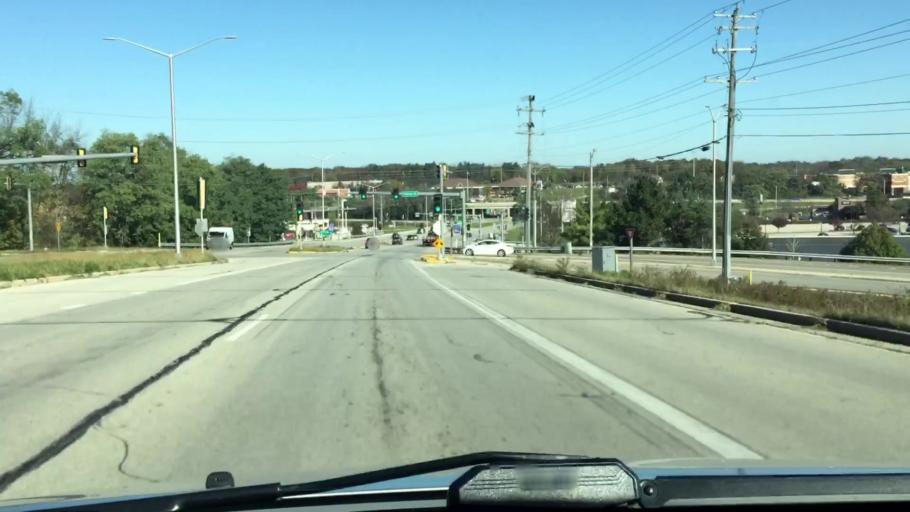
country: US
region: Wisconsin
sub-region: Waukesha County
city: Delafield
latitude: 43.0472
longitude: -88.3741
